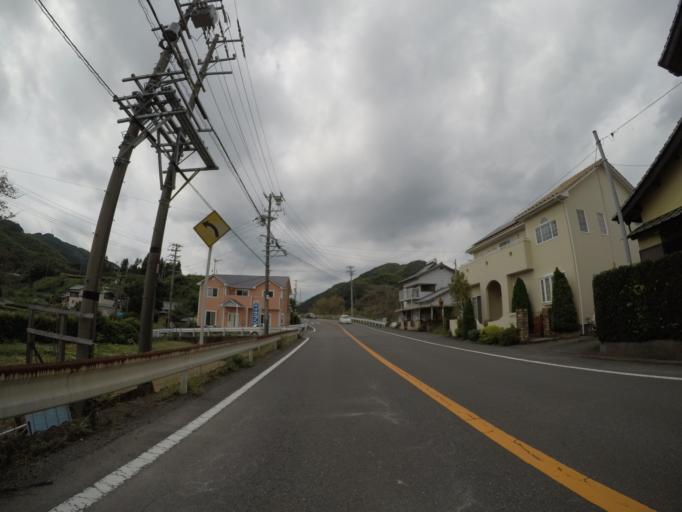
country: JP
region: Shizuoka
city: Fujieda
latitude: 34.8944
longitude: 138.2140
